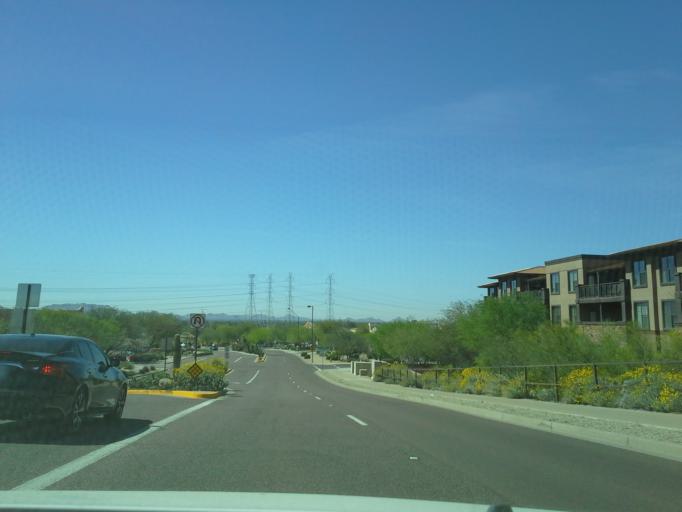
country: US
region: Arizona
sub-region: Maricopa County
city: Scottsdale
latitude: 33.5898
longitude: -111.8328
